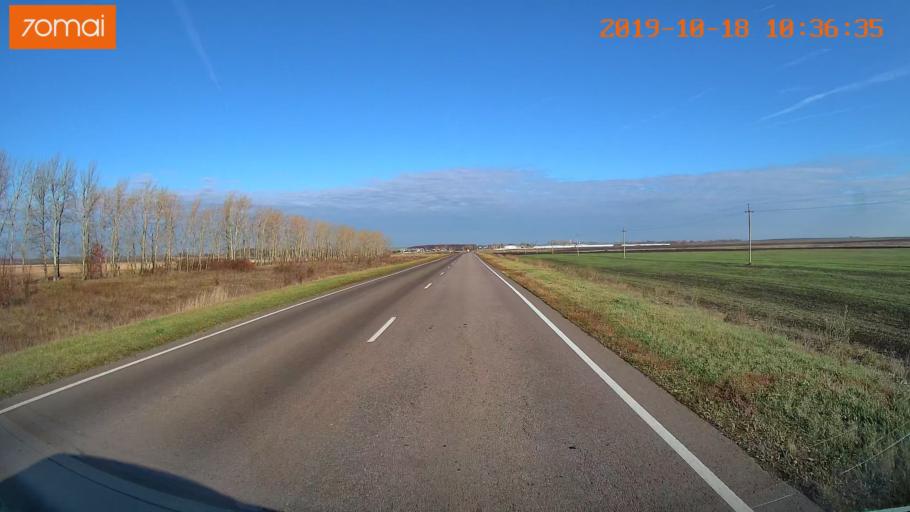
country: RU
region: Tula
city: Kurkino
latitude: 53.5503
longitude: 38.6265
